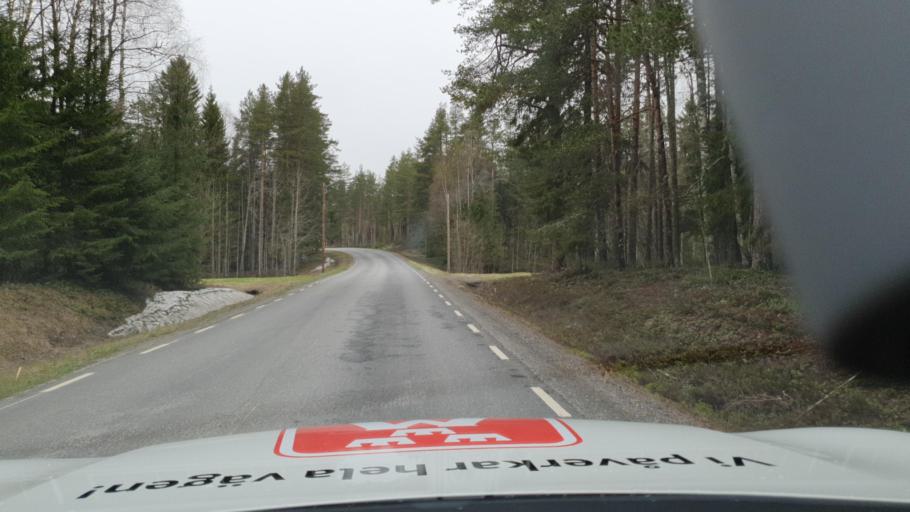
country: SE
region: Vaesterbotten
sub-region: Nordmalings Kommun
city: Nordmaling
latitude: 63.7059
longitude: 19.6043
